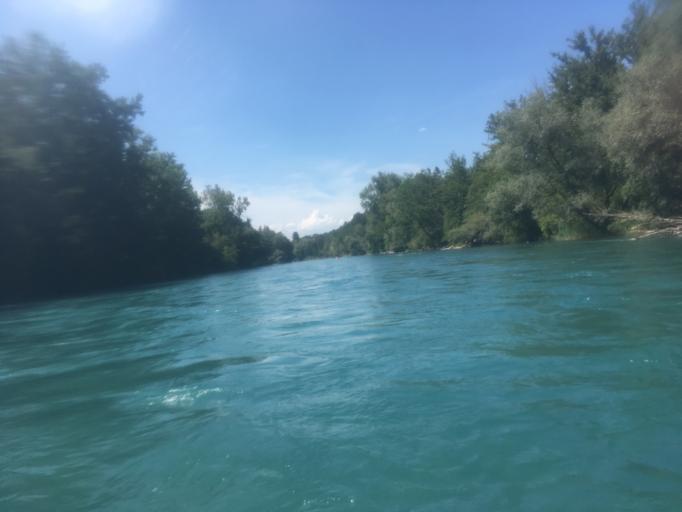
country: CH
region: Bern
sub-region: Bern-Mittelland District
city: Rubigen
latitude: 46.9008
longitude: 7.5267
